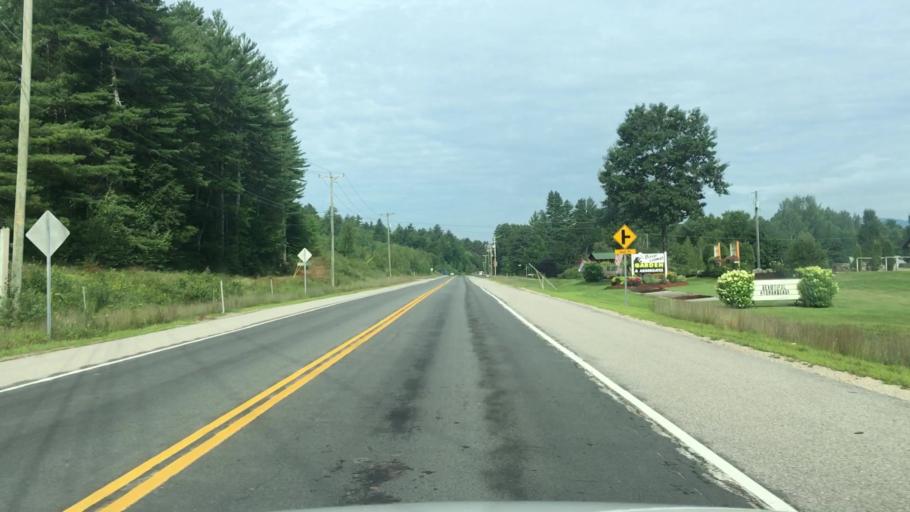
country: US
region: New Hampshire
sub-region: Carroll County
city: Tamworth
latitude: 43.8199
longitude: -71.2109
